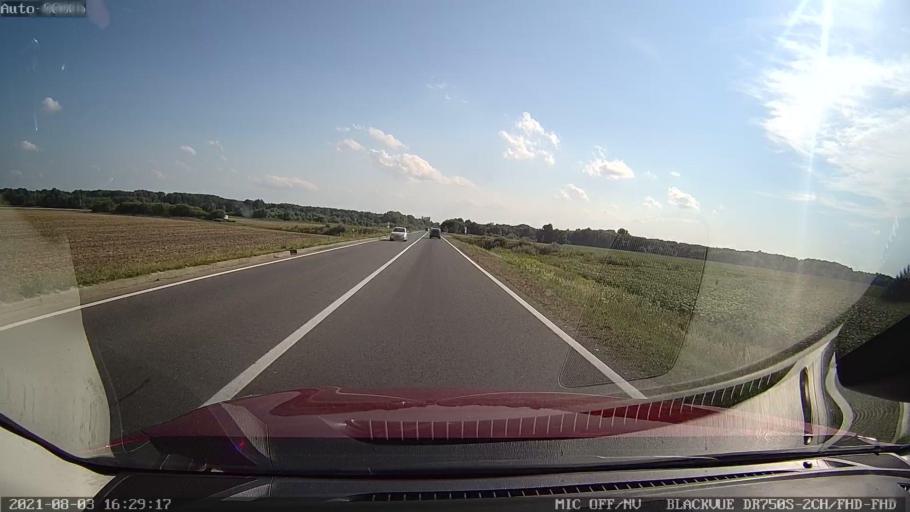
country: HR
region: Osjecko-Baranjska
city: Darda
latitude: 45.5988
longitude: 18.6566
